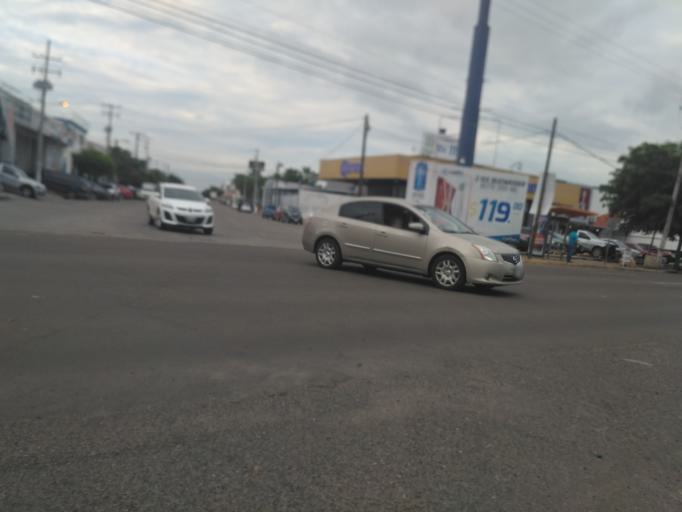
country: MX
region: Sinaloa
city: Culiacan
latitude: 24.7957
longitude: -107.4046
